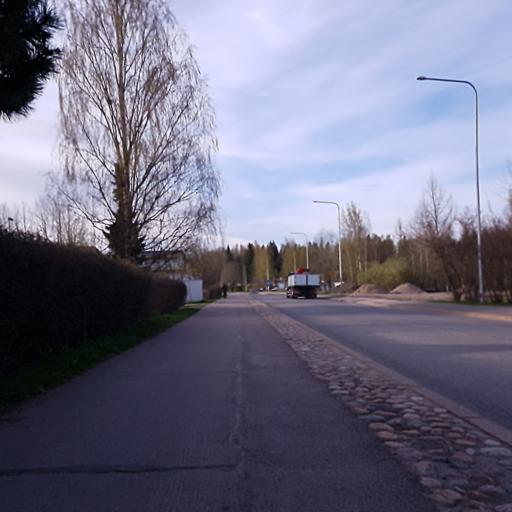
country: FI
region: Uusimaa
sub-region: Helsinki
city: Helsinki
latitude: 60.2555
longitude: 24.9380
